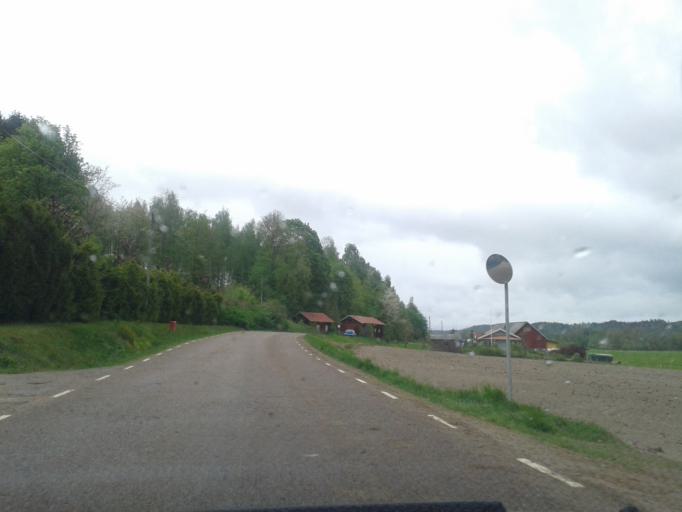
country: SE
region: Vaestra Goetaland
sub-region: Lilla Edets Kommun
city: Lodose
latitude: 58.0224
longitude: 12.1357
